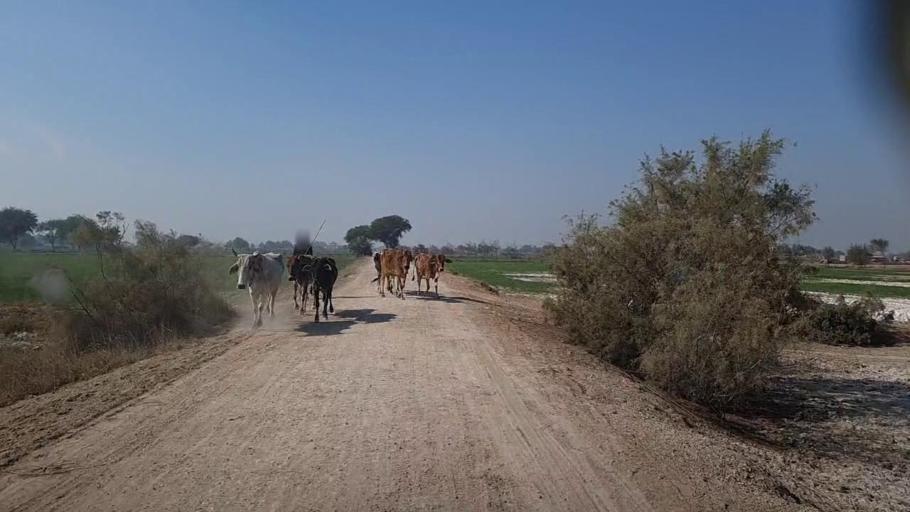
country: PK
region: Sindh
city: Khairpur
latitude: 27.9938
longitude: 69.6989
